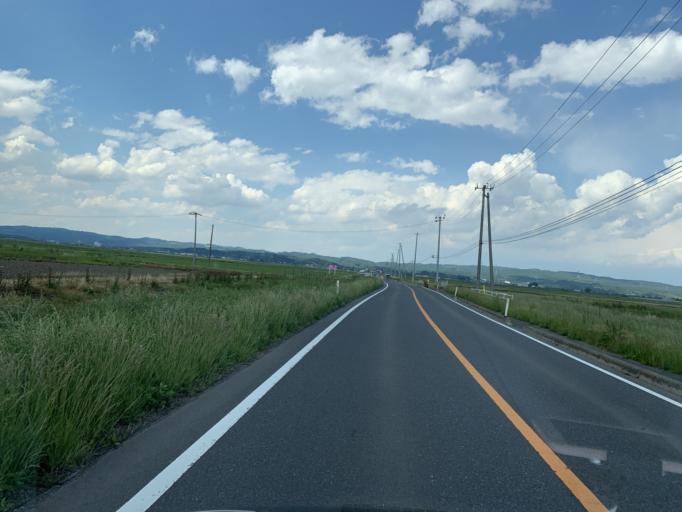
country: JP
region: Miyagi
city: Wakuya
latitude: 38.5149
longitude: 141.1262
